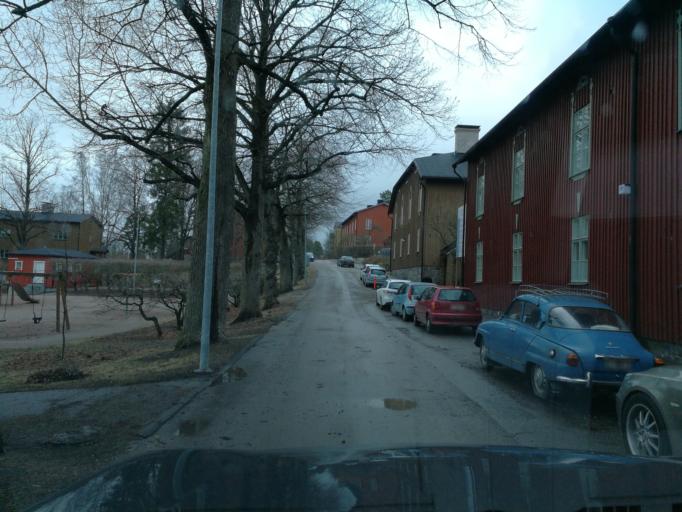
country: FI
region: Uusimaa
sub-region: Helsinki
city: Helsinki
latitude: 60.2137
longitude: 24.9492
